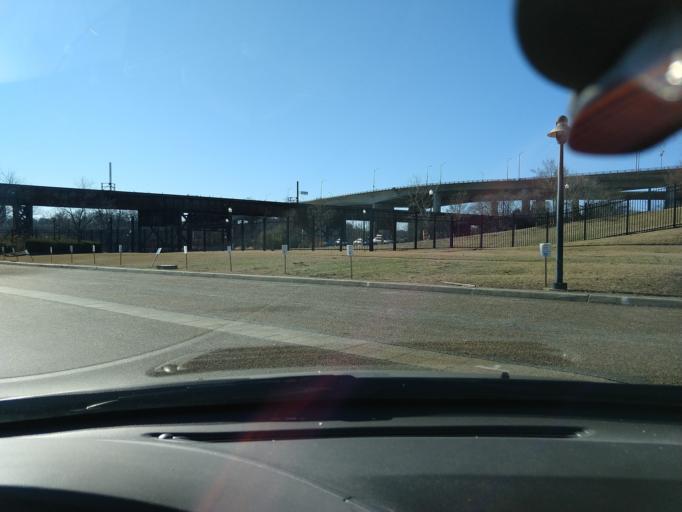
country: US
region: Virginia
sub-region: City of Richmond
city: Richmond
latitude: 37.5353
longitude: -77.4467
